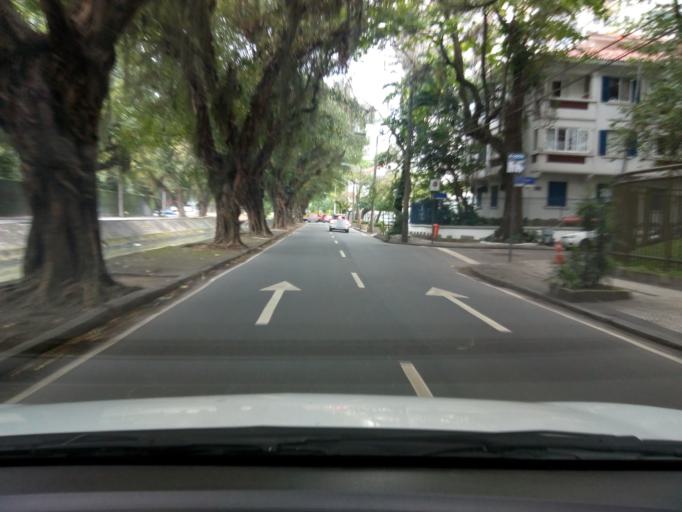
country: BR
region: Rio de Janeiro
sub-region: Rio De Janeiro
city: Rio de Janeiro
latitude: -22.9831
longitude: -43.2274
